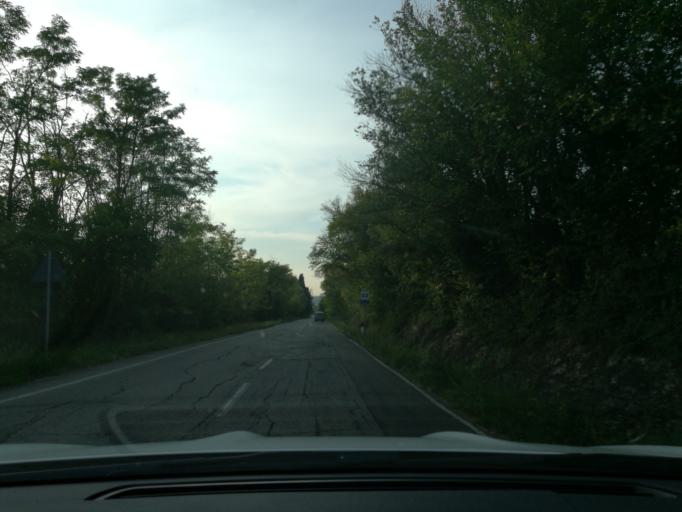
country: IT
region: Umbria
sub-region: Provincia di Terni
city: San Gemini
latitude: 42.6363
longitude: 12.5480
